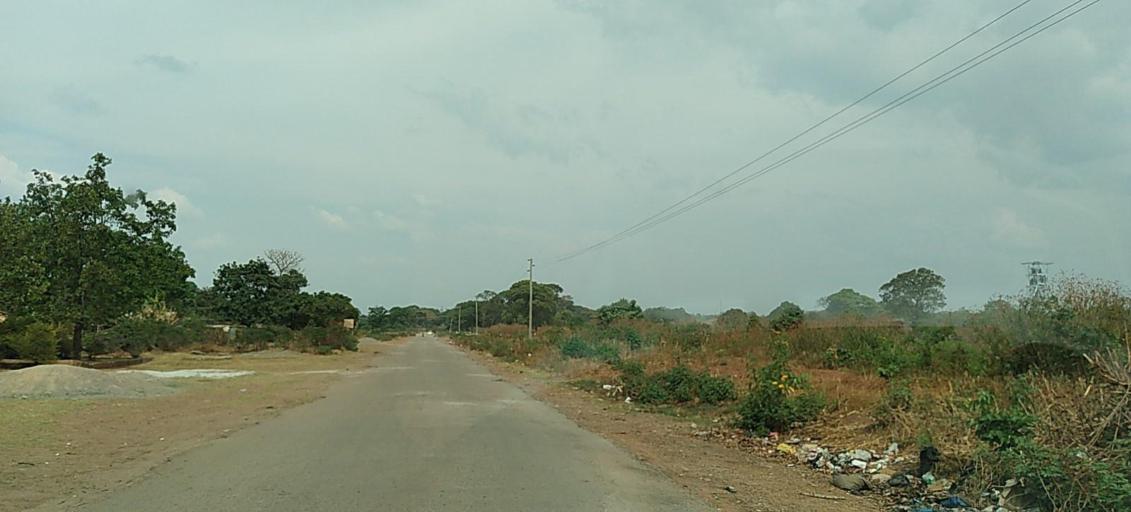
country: ZM
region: Copperbelt
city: Chililabombwe
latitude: -12.3732
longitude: 27.8221
